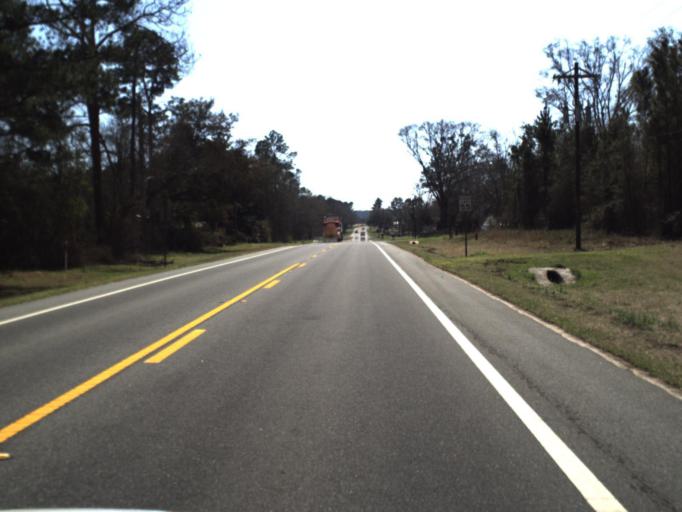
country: US
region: Florida
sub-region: Jackson County
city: Sneads
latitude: 30.7019
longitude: -85.0203
